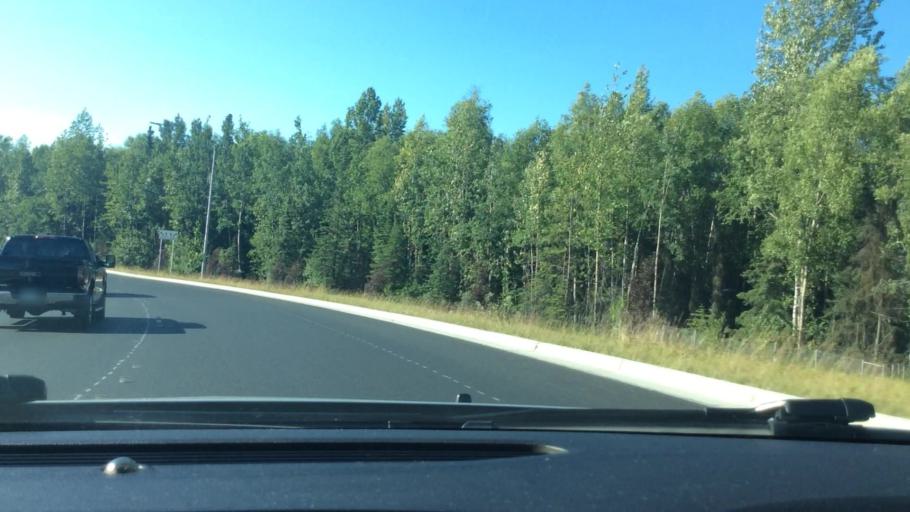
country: US
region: Alaska
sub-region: Anchorage Municipality
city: Elmendorf Air Force Base
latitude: 61.2301
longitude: -149.7338
